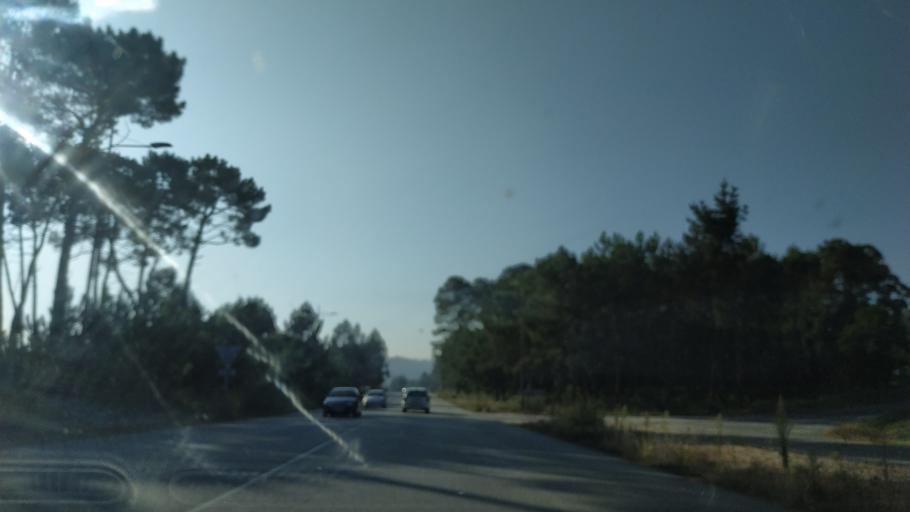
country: ES
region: Galicia
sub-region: Provincia da Coruna
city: Carballo
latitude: 43.2312
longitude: -8.6783
